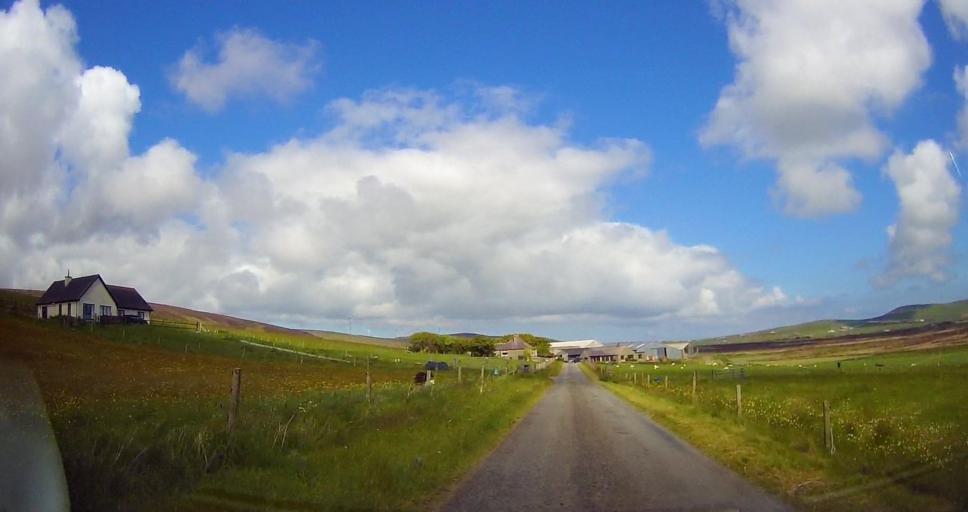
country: GB
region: Scotland
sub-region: Orkney Islands
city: Orkney
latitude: 59.0555
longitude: -3.1023
